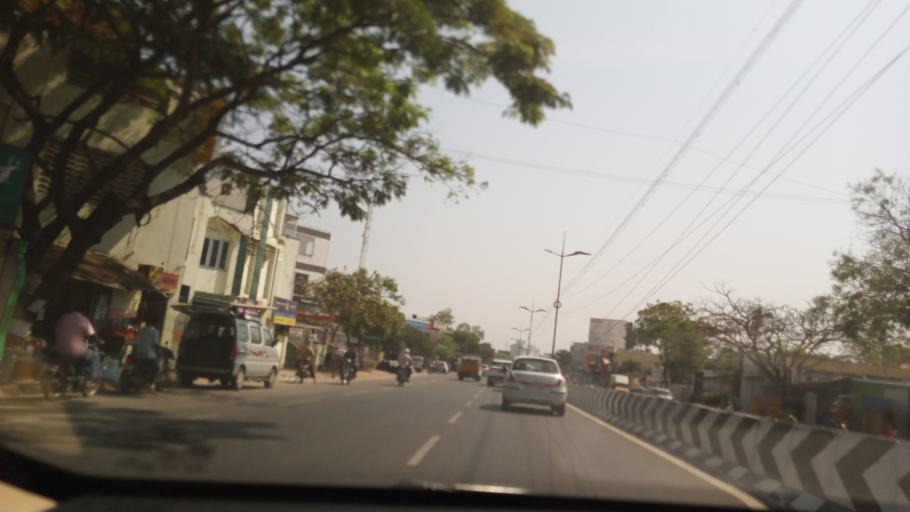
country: IN
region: Tamil Nadu
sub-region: Coimbatore
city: Irugur
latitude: 11.0532
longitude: 77.0620
